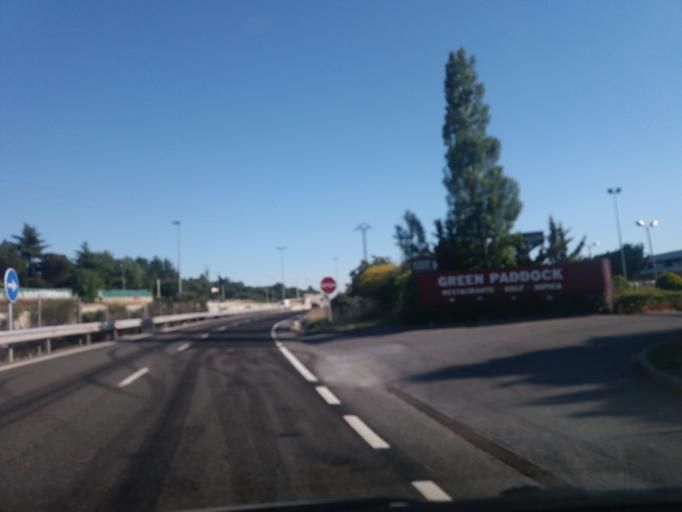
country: ES
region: Madrid
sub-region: Provincia de Madrid
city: Torrelodones
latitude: 40.5935
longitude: -3.9529
